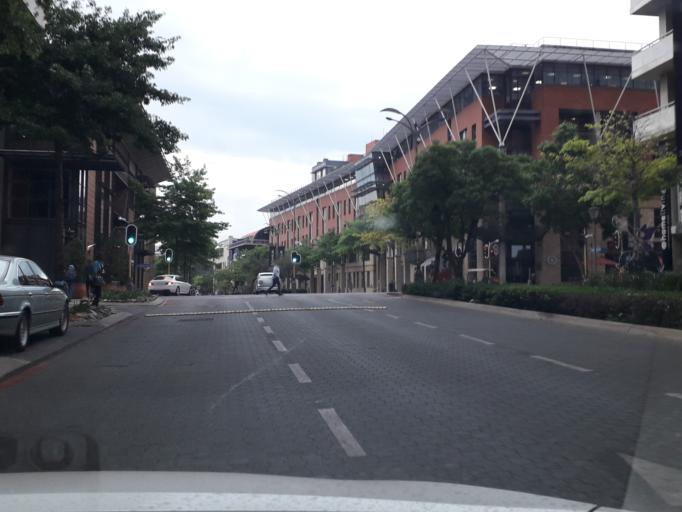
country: ZA
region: Gauteng
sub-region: City of Johannesburg Metropolitan Municipality
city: Johannesburg
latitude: -26.1325
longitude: 28.0692
